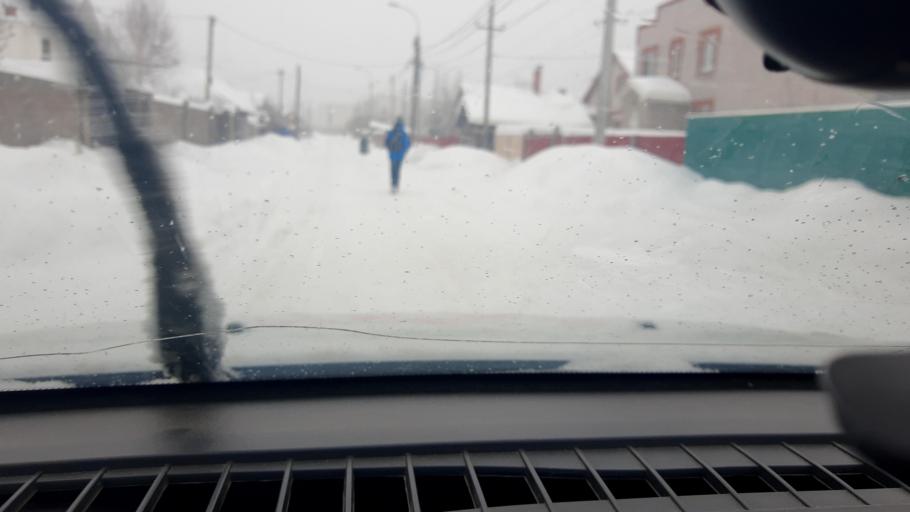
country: RU
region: Bashkortostan
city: Ufa
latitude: 54.6690
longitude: 55.9385
